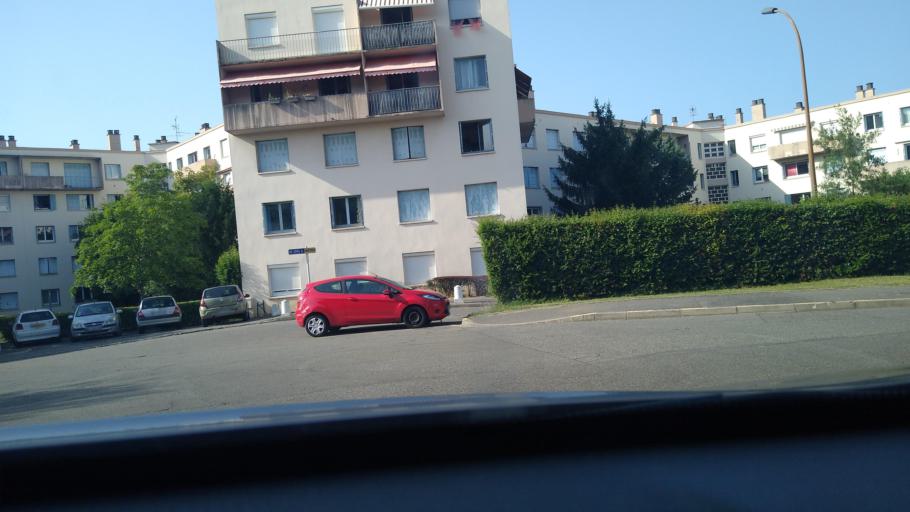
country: FR
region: Midi-Pyrenees
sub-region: Departement de la Haute-Garonne
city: Toulouse
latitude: 43.6136
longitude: 1.4630
